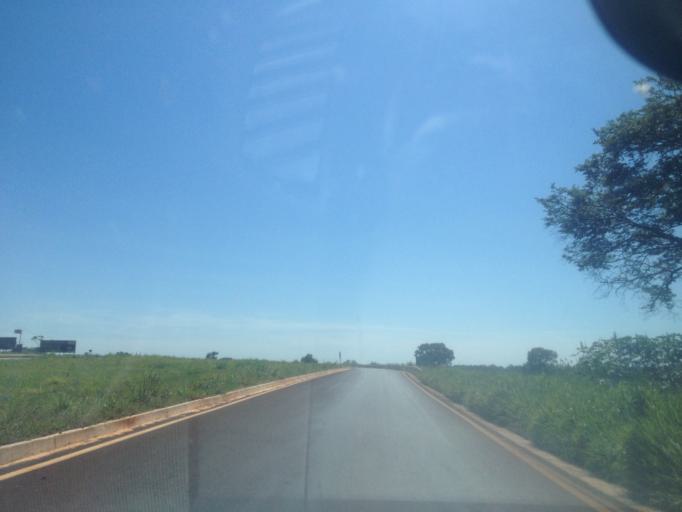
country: BR
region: Minas Gerais
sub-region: Santa Vitoria
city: Santa Vitoria
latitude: -18.8768
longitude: -50.1239
